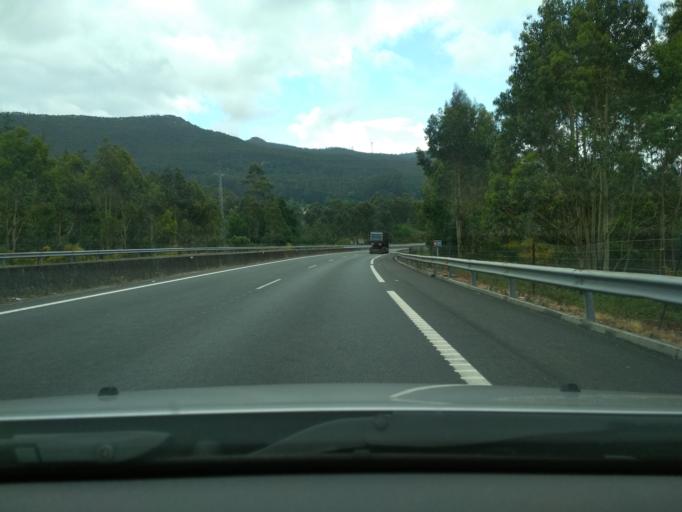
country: ES
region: Galicia
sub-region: Provincia da Coruna
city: Padron
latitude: 42.7796
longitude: -8.6430
